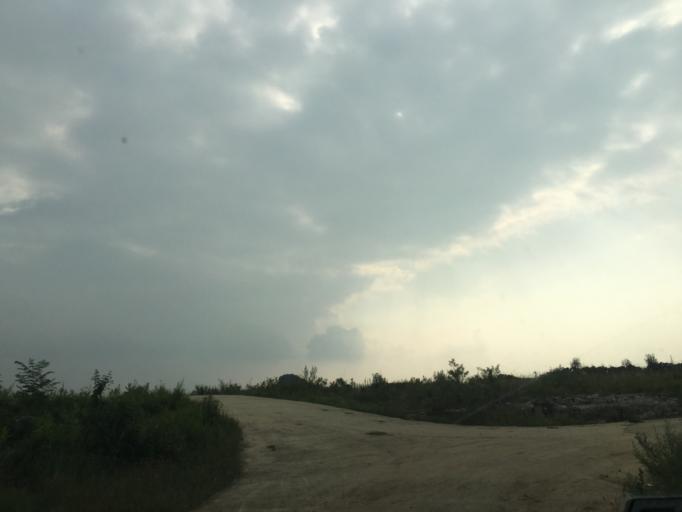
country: CN
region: Guangxi Zhuangzu Zizhiqu
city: Xinzhou
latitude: 25.4440
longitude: 105.6426
